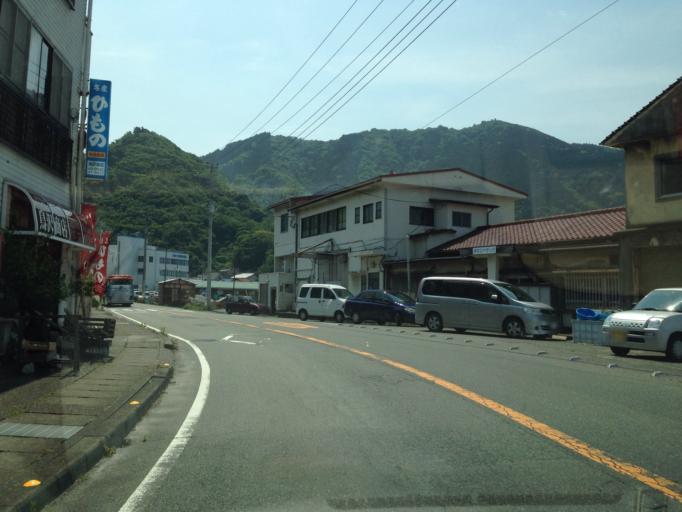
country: JP
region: Shizuoka
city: Numazu
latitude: 35.0261
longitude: 138.8971
